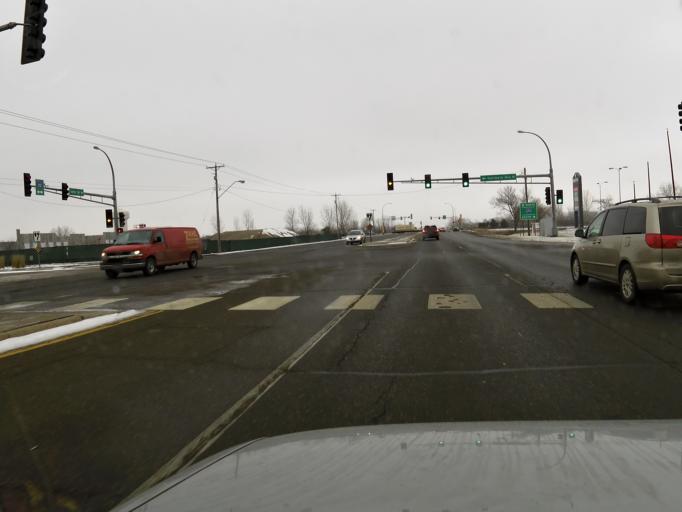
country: US
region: Minnesota
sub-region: Washington County
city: Oakdale
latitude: 44.9631
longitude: -92.9624
